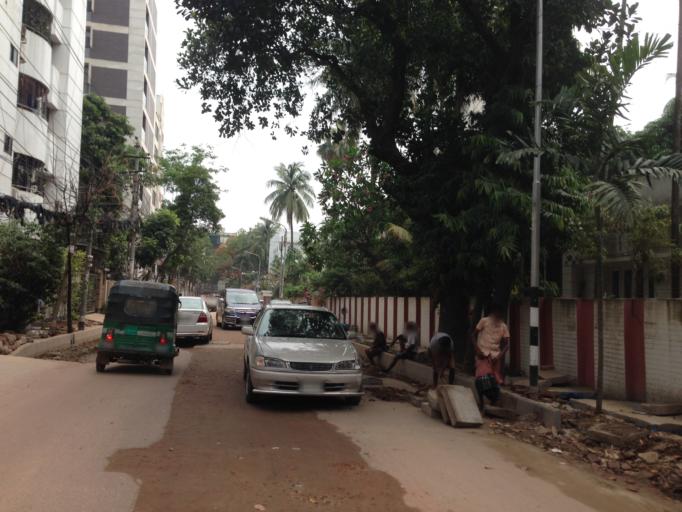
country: BD
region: Dhaka
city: Paltan
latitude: 23.7790
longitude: 90.4138
